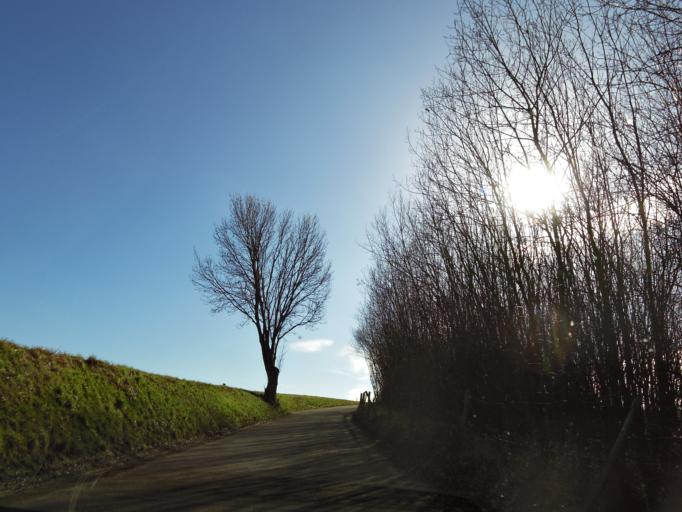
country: NL
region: Limburg
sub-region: Valkenburg aan de Geul
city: Schin op Geul
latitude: 50.8066
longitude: 5.8860
